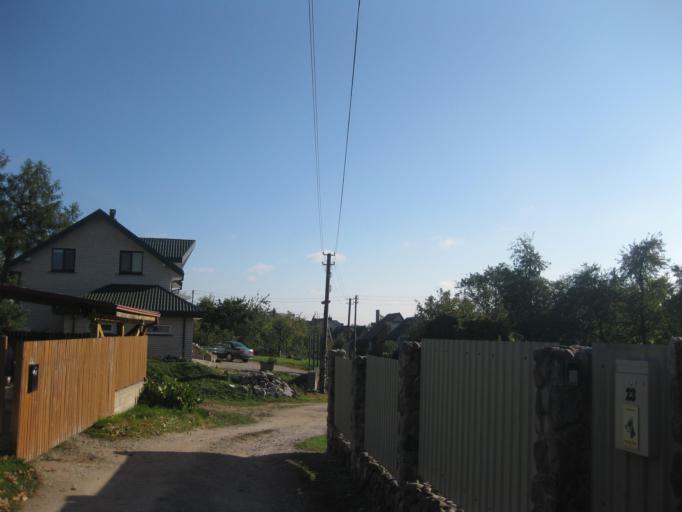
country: LT
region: Kauno apskritis
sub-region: Kauno rajonas
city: Garliava
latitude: 54.8355
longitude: 23.8653
